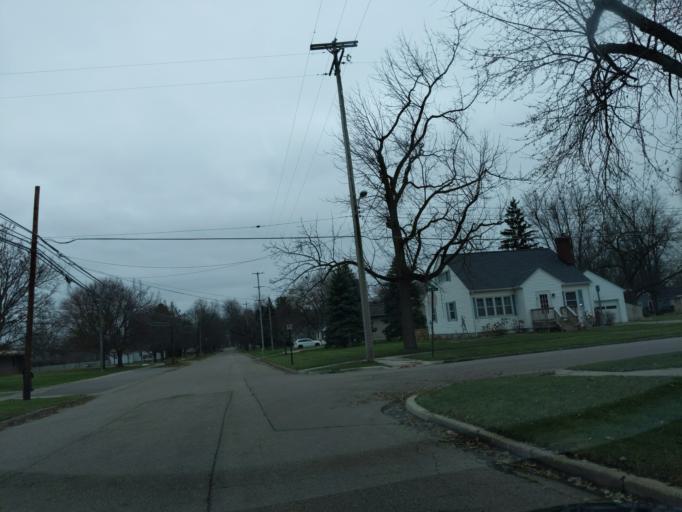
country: US
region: Michigan
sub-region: Clinton County
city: Saint Johns
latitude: 42.9982
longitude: -84.5527
